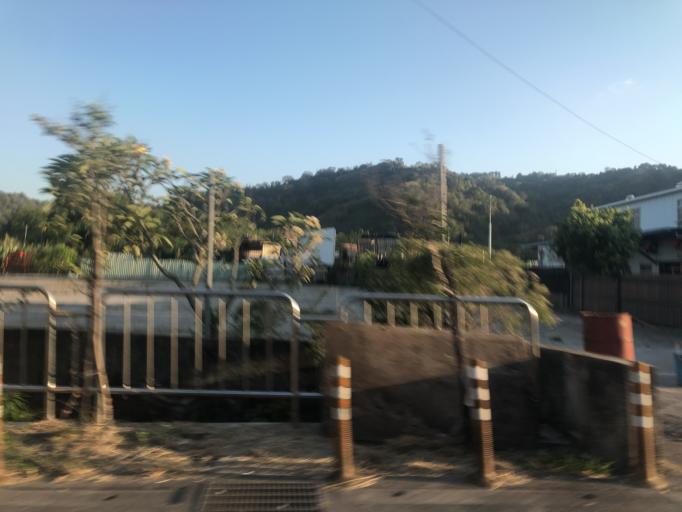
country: TW
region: Taiwan
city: Fengyuan
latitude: 24.2785
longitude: 120.7694
